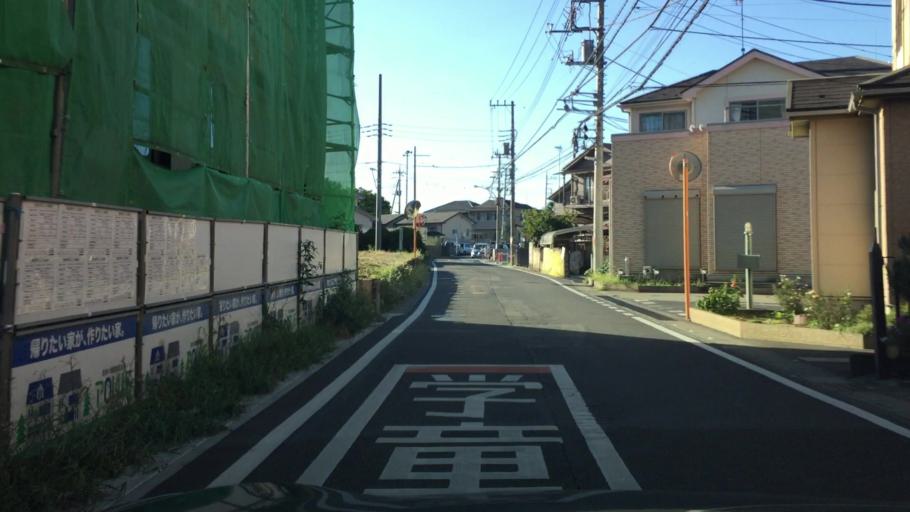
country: JP
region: Saitama
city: Ageoshimo
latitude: 35.9204
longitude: 139.5865
